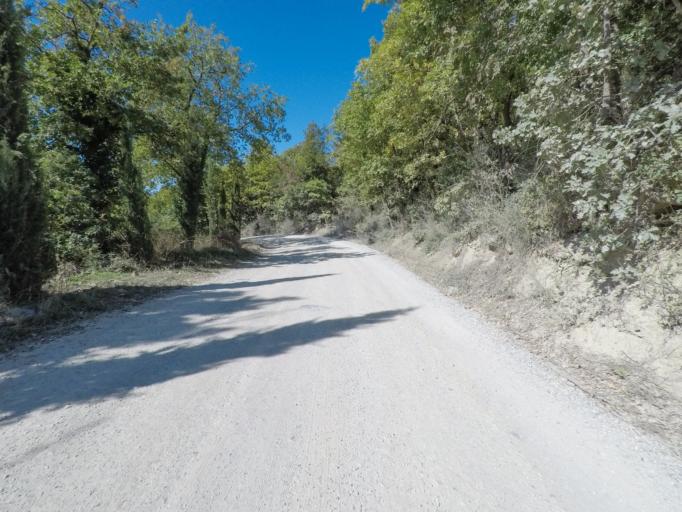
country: IT
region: Tuscany
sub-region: Provincia di Siena
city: Castellina in Chianti
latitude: 43.4363
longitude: 11.3293
